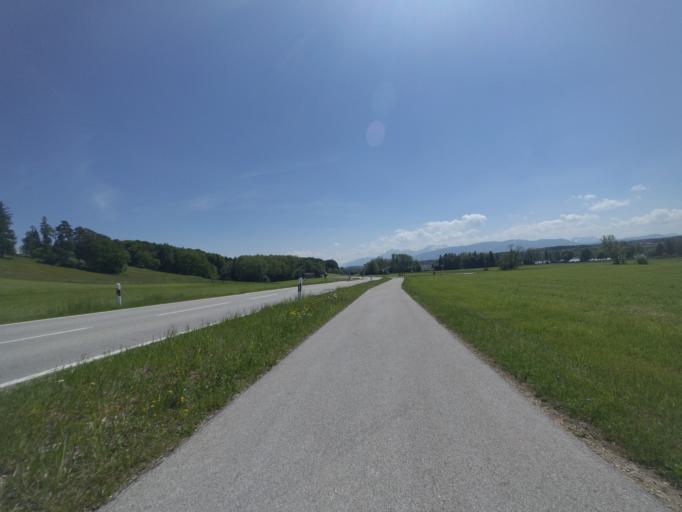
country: DE
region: Bavaria
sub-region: Upper Bavaria
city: Petting
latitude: 47.9320
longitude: 12.8059
